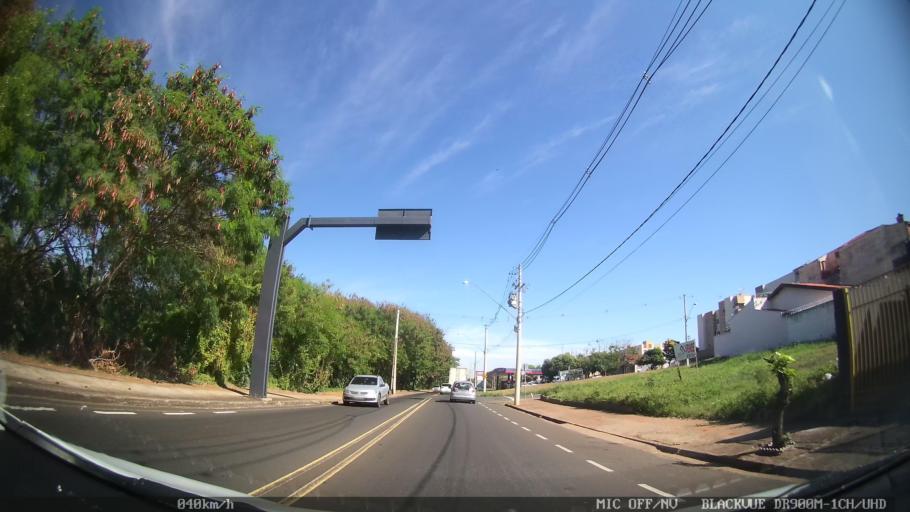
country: BR
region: Sao Paulo
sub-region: Sao Jose Do Rio Preto
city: Sao Jose do Rio Preto
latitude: -20.8030
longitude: -49.4101
